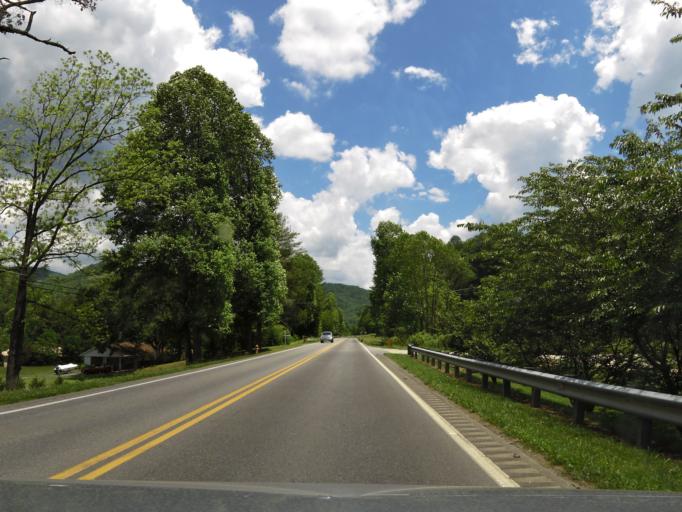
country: US
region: North Carolina
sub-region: Graham County
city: Robbinsville
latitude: 35.2924
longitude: -83.7805
